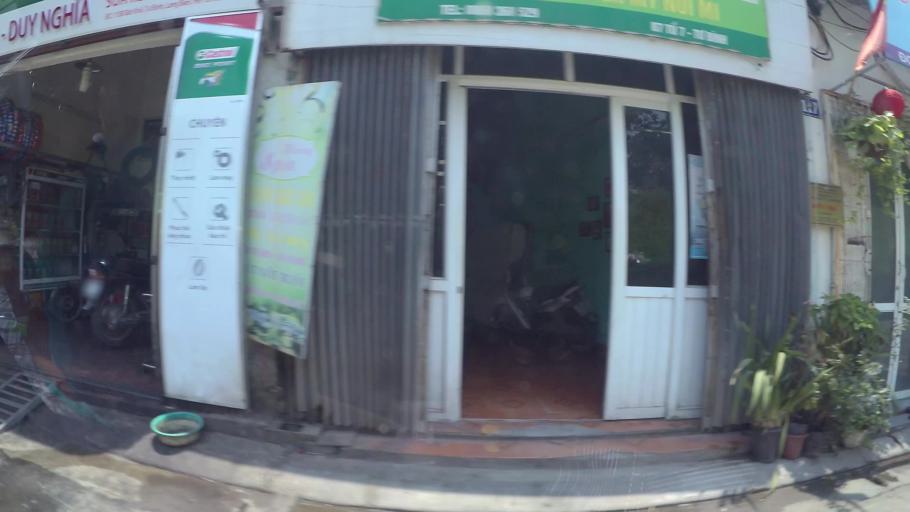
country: VN
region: Ha Noi
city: Hoan Kiem
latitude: 21.0250
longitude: 105.8849
